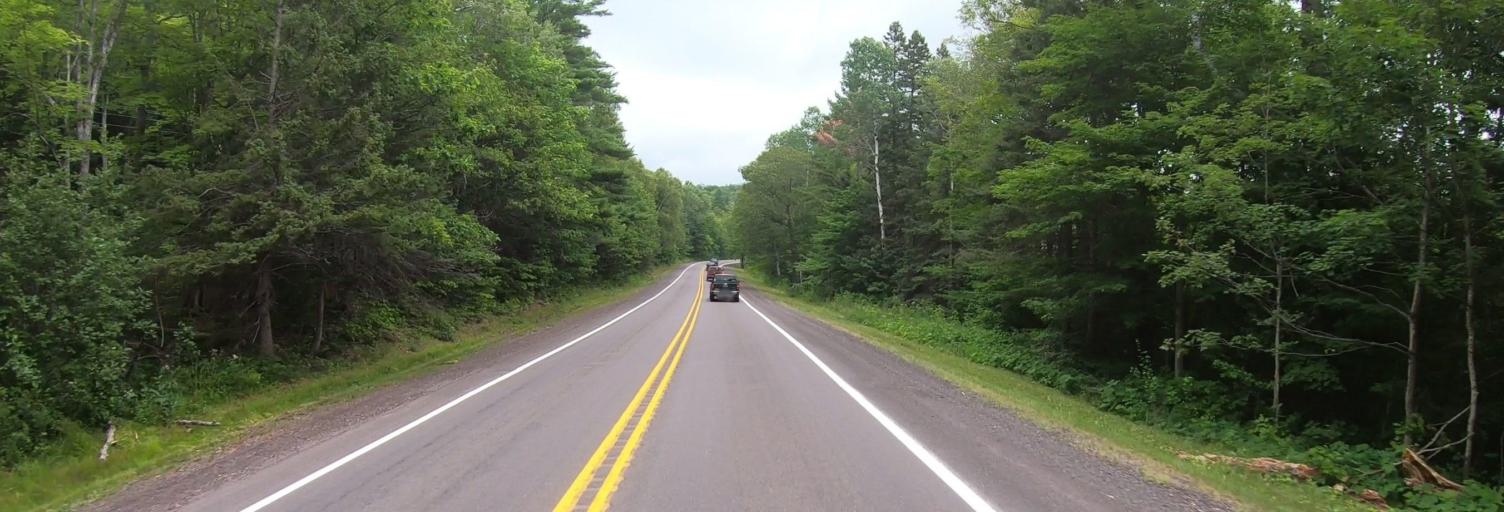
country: US
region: Michigan
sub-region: Keweenaw County
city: Eagle River
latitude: 47.3971
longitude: -88.2546
